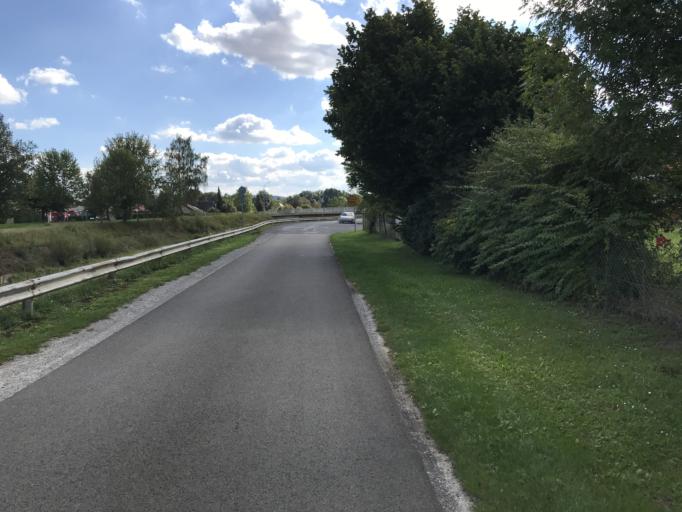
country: DE
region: Hesse
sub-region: Regierungsbezirk Kassel
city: Eschwege
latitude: 51.2022
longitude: 10.0024
